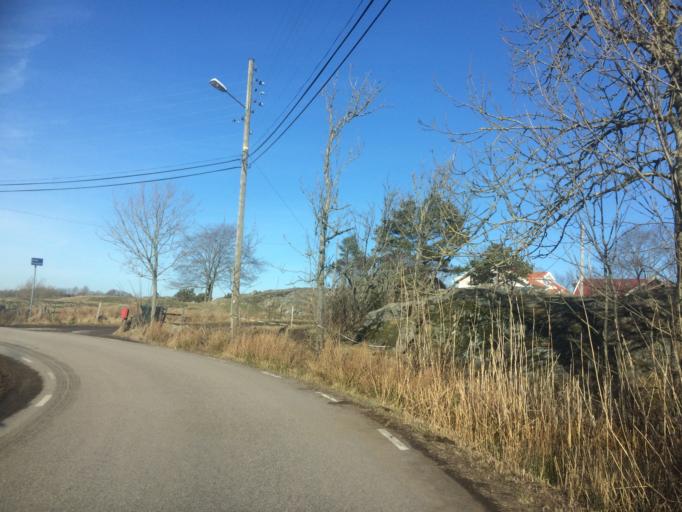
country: SE
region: Vaestra Goetaland
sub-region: Goteborg
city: Majorna
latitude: 57.7876
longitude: 11.8687
